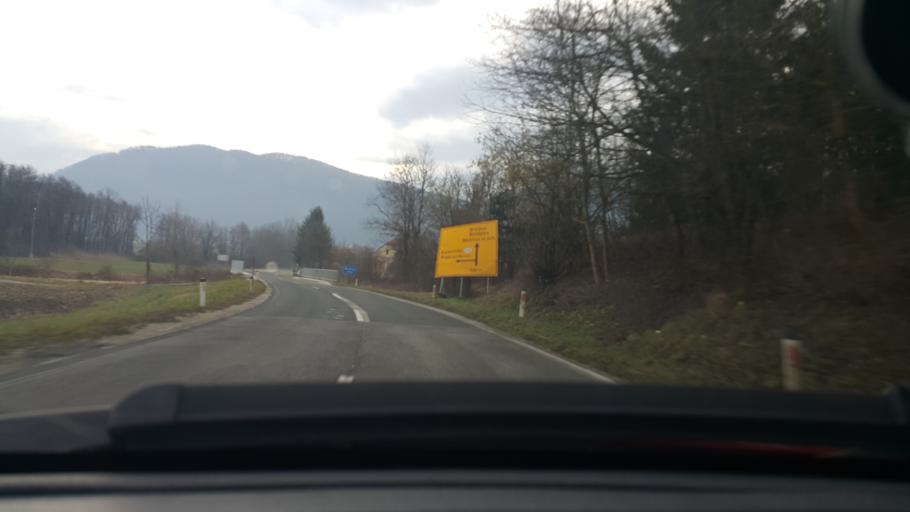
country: SI
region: Bistrica ob Sotli
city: Bistrica ob Sotli
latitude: 46.0637
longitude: 15.6525
